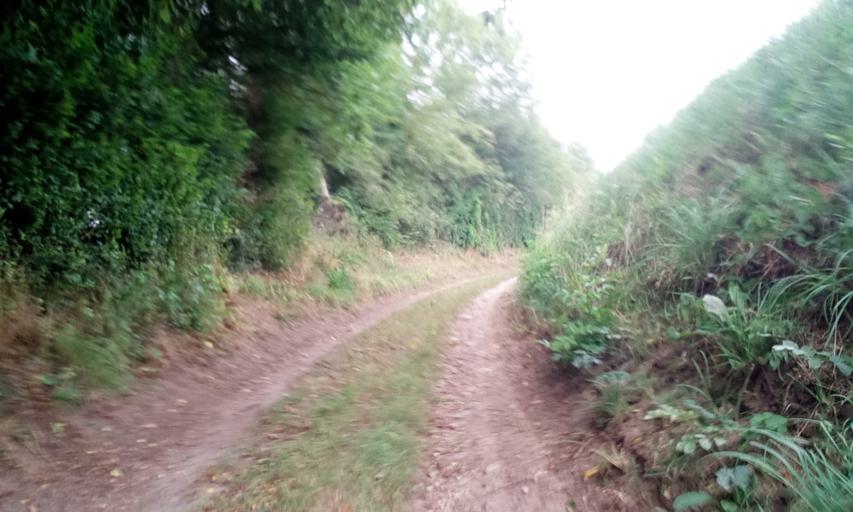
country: FR
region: Lower Normandy
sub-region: Departement du Calvados
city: Tilly-sur-Seulles
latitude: 49.2259
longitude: -0.6237
